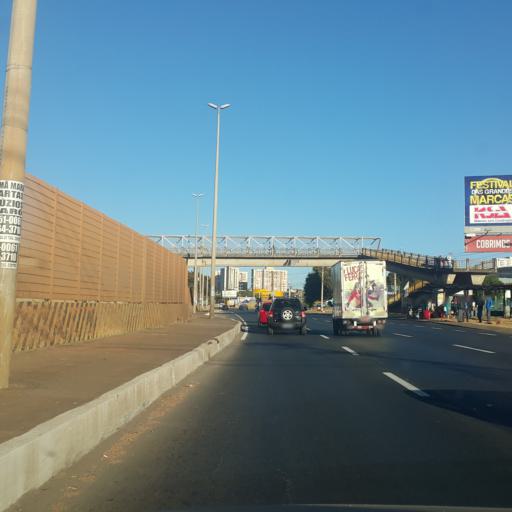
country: BR
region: Federal District
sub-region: Brasilia
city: Brasilia
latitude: -15.8343
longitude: -48.0803
